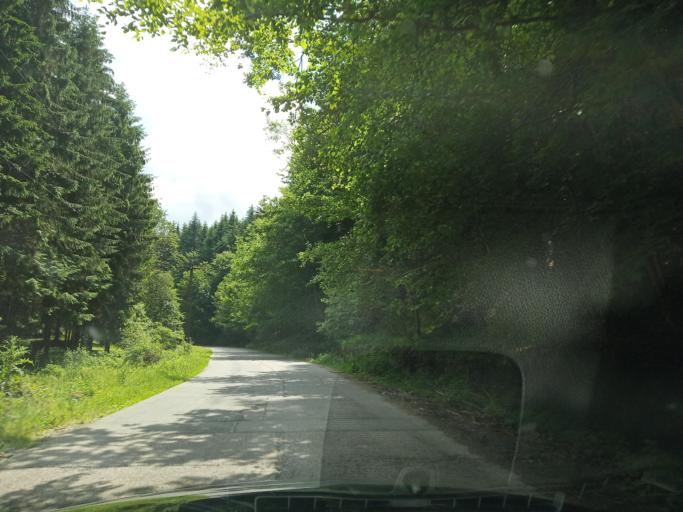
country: RO
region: Hunedoara
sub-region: Oras Petrila
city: Petrila
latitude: 45.3952
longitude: 23.4243
